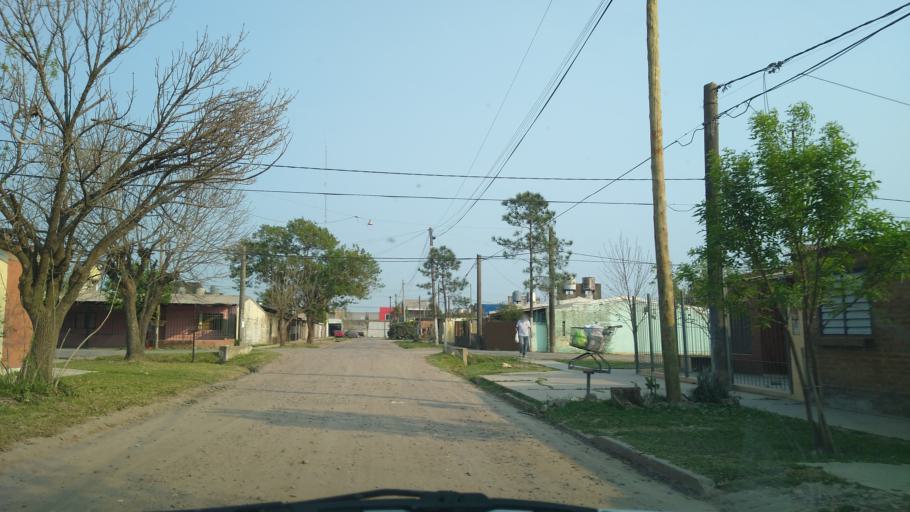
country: AR
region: Chaco
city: Resistencia
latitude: -27.4836
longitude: -58.9778
